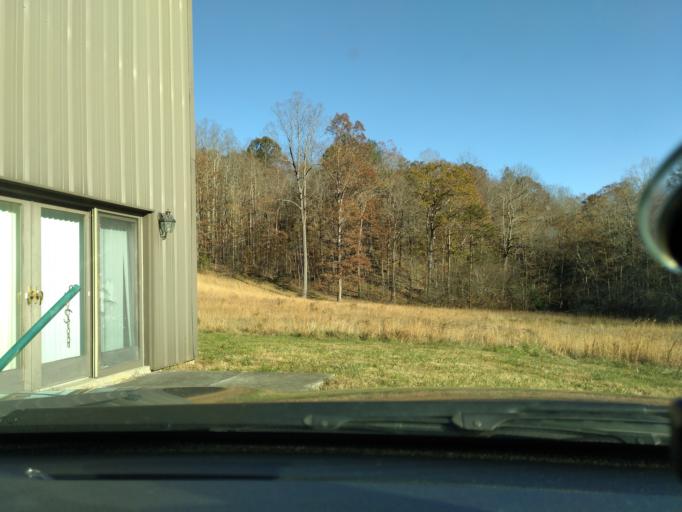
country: US
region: Virginia
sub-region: Floyd County
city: Floyd
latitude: 36.8324
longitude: -80.1783
